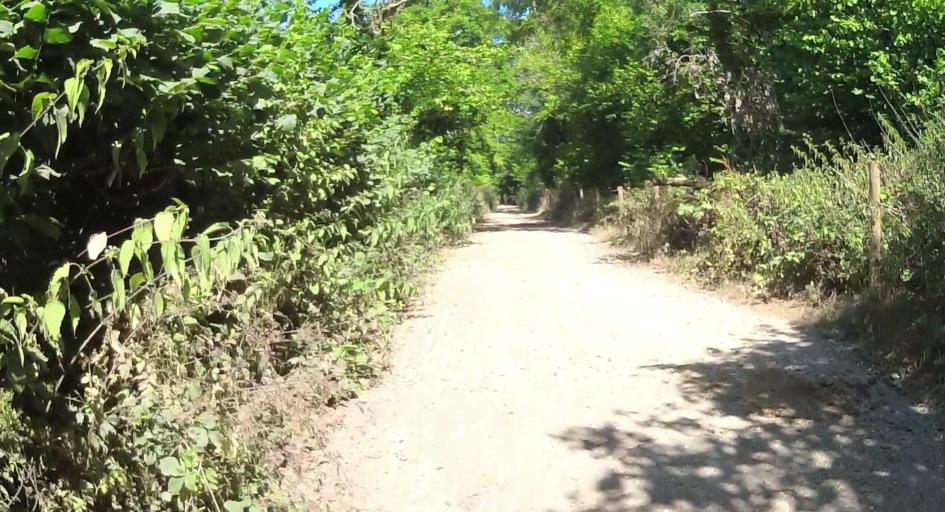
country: GB
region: England
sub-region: Dorset
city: Bovington Camp
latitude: 50.7056
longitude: -2.2754
